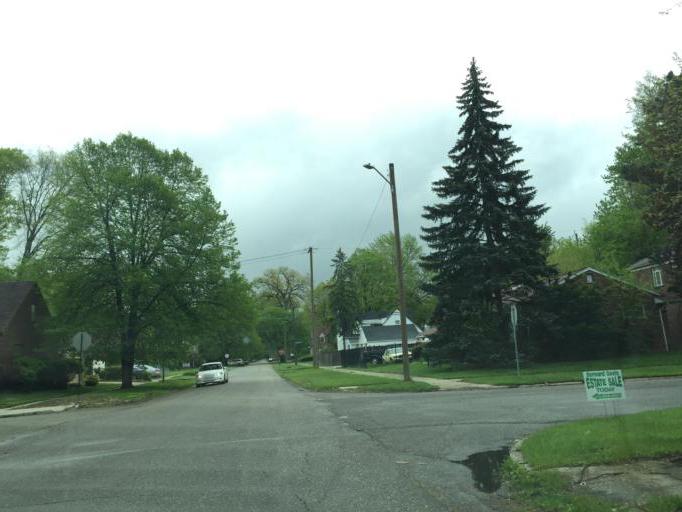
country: US
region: Michigan
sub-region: Wayne County
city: Redford
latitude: 42.3936
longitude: -83.2312
